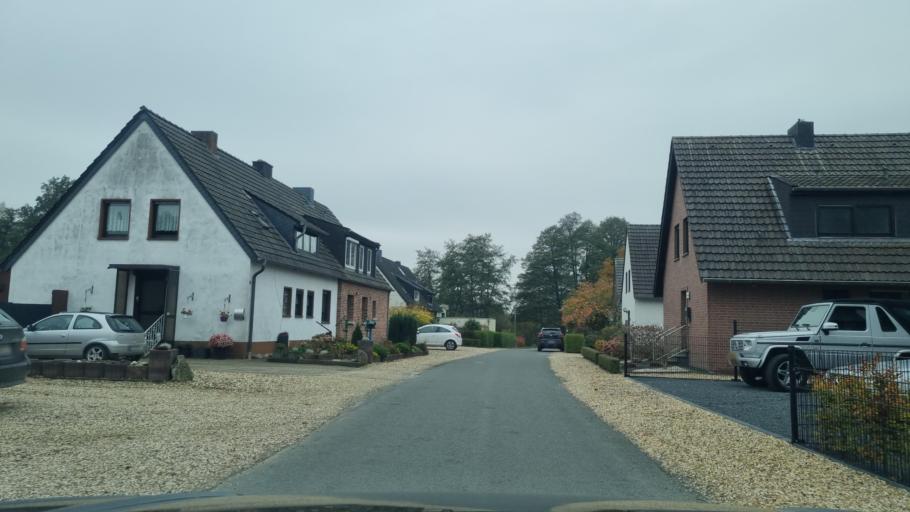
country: DE
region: North Rhine-Westphalia
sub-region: Regierungsbezirk Dusseldorf
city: Kranenburg
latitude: 51.7937
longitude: 6.0694
